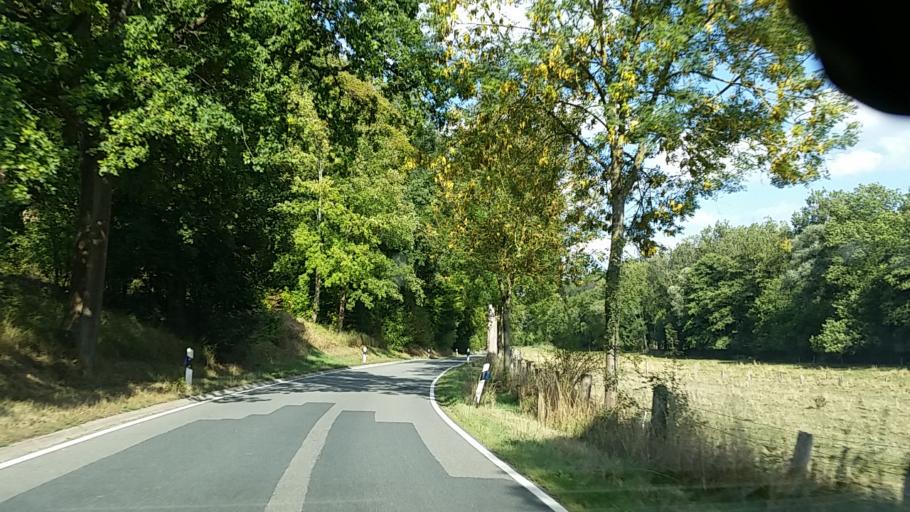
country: DE
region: Lower Saxony
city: Juhnde
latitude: 51.4368
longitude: 9.8444
